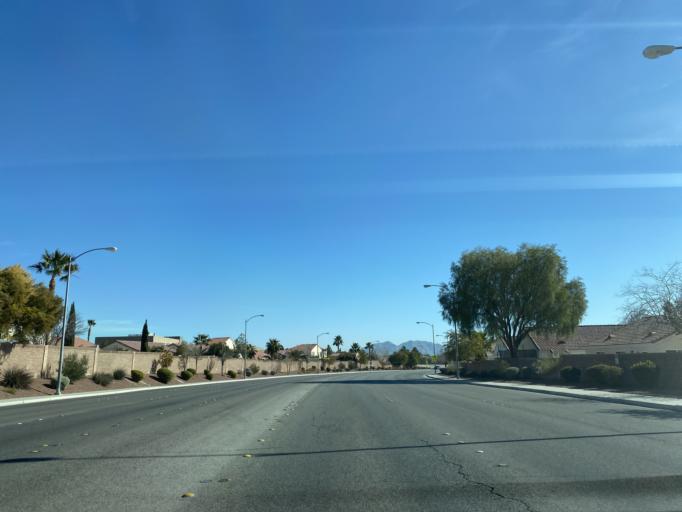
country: US
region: Nevada
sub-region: Clark County
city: North Las Vegas
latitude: 36.2816
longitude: -115.1463
